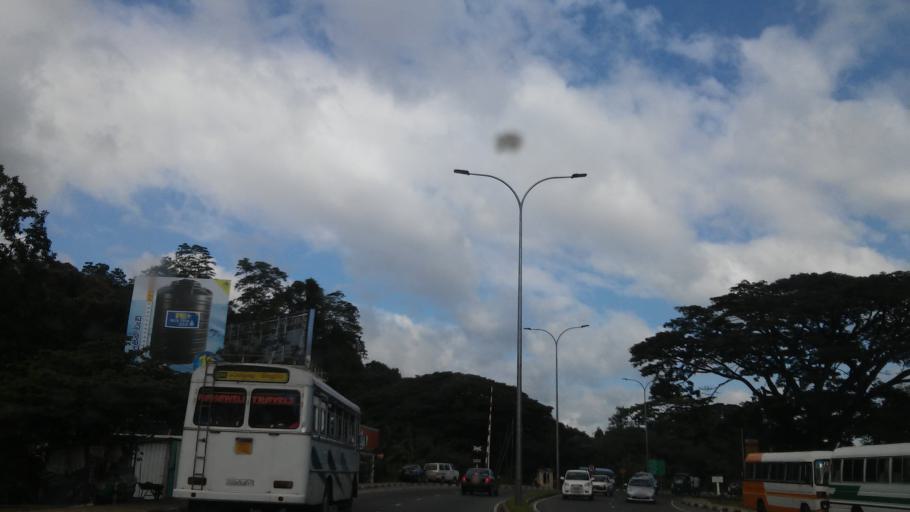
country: LK
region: Central
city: Kandy
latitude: 7.2715
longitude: 80.6073
